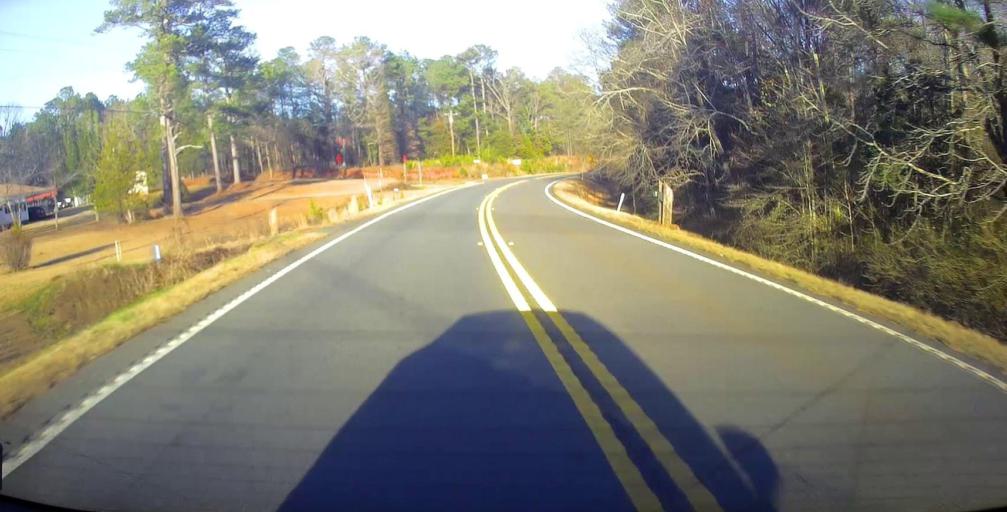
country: US
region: Georgia
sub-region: Upson County
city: Thomaston
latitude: 32.8619
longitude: -84.4130
